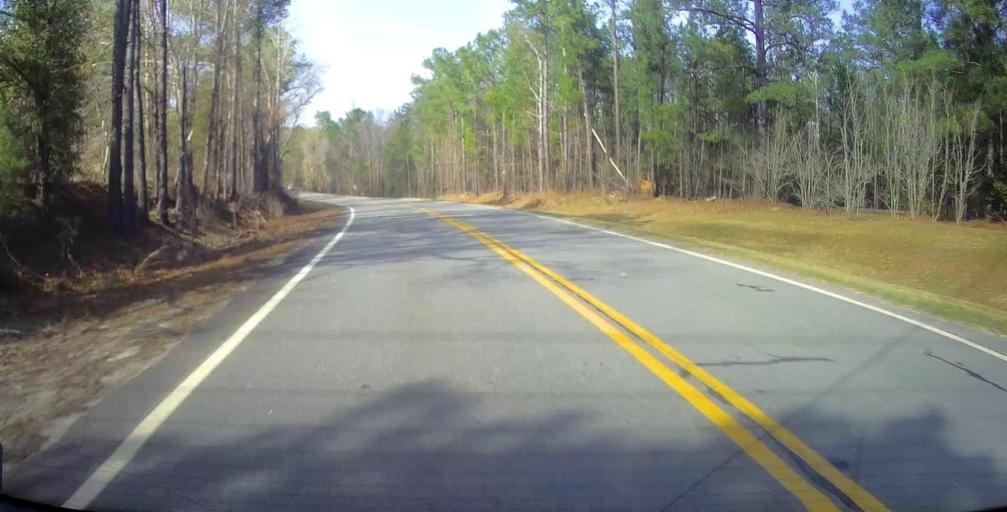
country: US
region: Georgia
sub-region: Wilkinson County
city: Gordon
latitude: 32.7854
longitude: -83.3299
